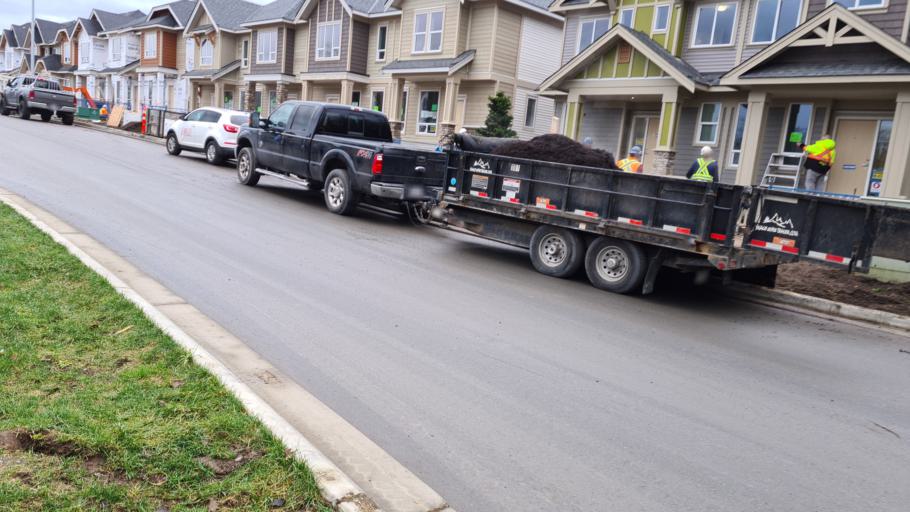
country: CA
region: British Columbia
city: Walnut Grove
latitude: 49.1445
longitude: -122.6568
